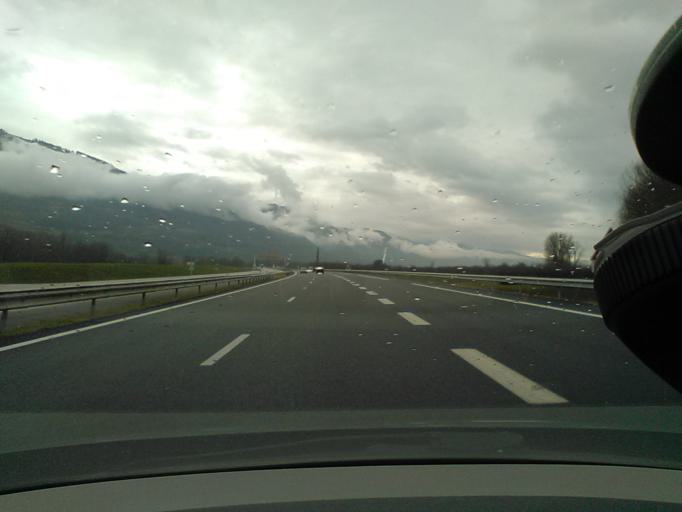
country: FR
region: Rhone-Alpes
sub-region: Departement de l'Isere
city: Pontcharra
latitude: 45.4229
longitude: 5.9977
